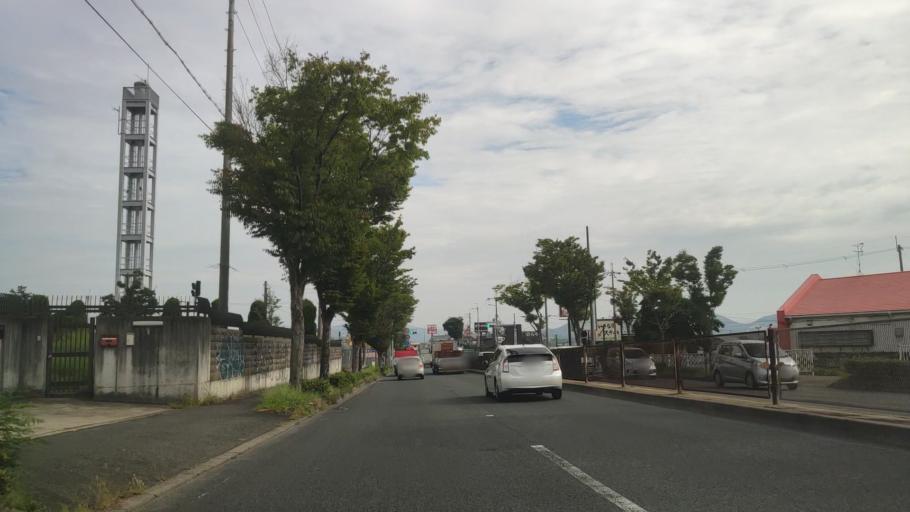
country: JP
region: Osaka
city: Tondabayashicho
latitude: 34.5117
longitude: 135.6029
